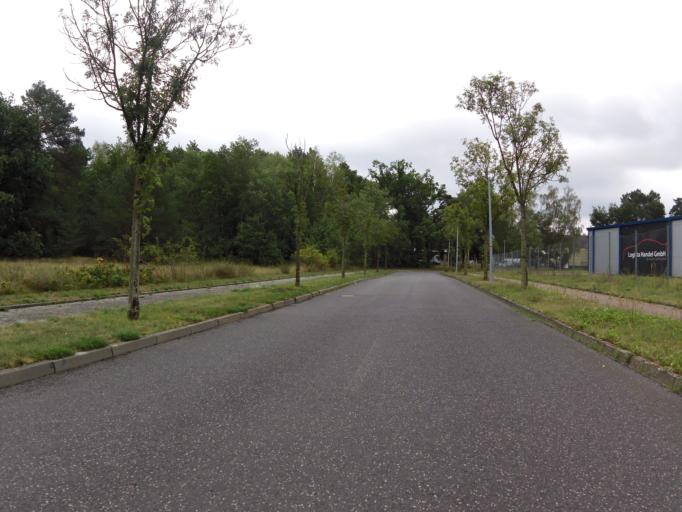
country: DE
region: Brandenburg
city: Storkow
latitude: 52.2684
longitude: 13.9489
